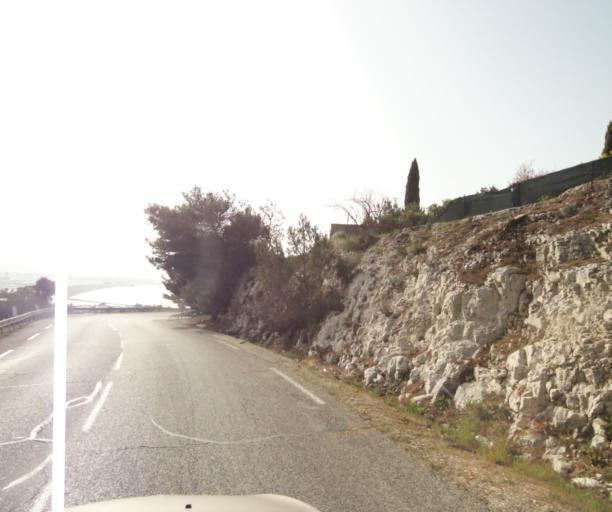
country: FR
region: Provence-Alpes-Cote d'Azur
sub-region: Departement des Bouches-du-Rhone
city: Vitrolles
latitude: 43.4623
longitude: 5.2379
